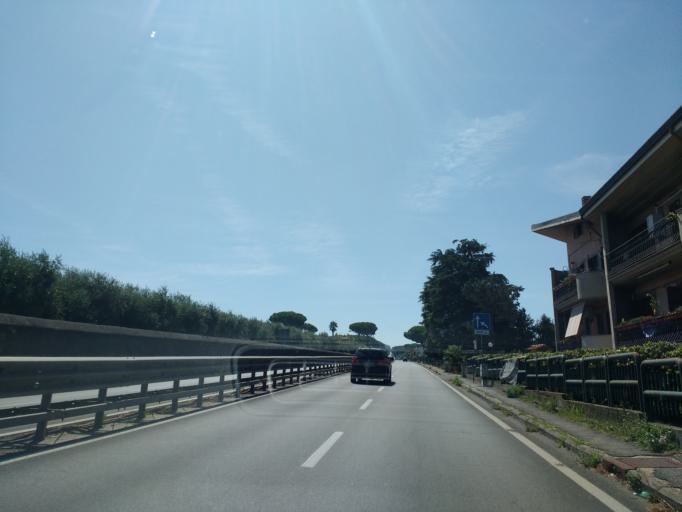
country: IT
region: Latium
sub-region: Citta metropolitana di Roma Capitale
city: Marino
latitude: 41.7640
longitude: 12.6193
